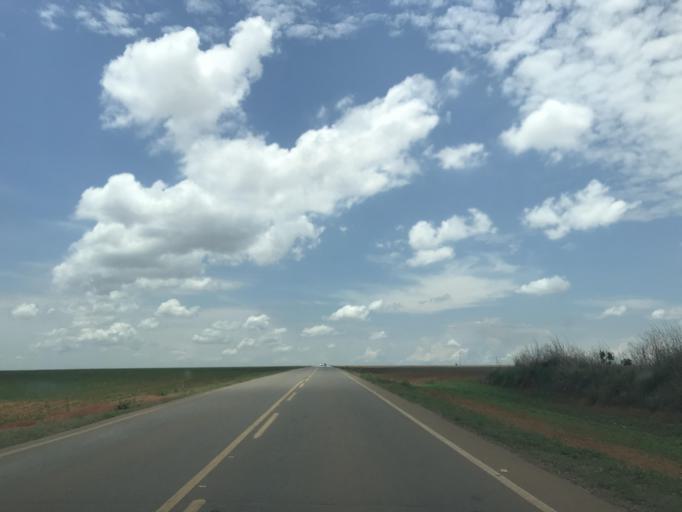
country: BR
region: Goias
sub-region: Vianopolis
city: Vianopolis
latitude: -16.5130
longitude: -48.2338
